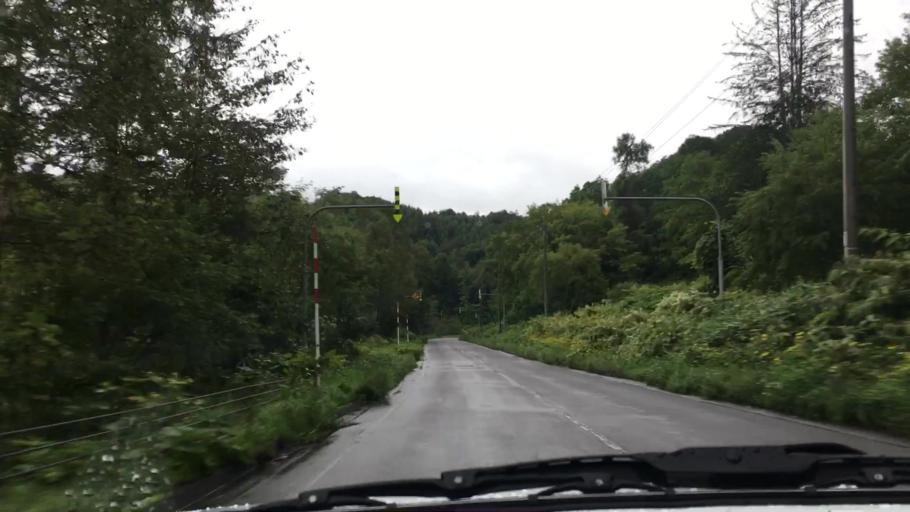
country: JP
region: Hokkaido
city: Niseko Town
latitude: 42.6652
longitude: 140.7774
